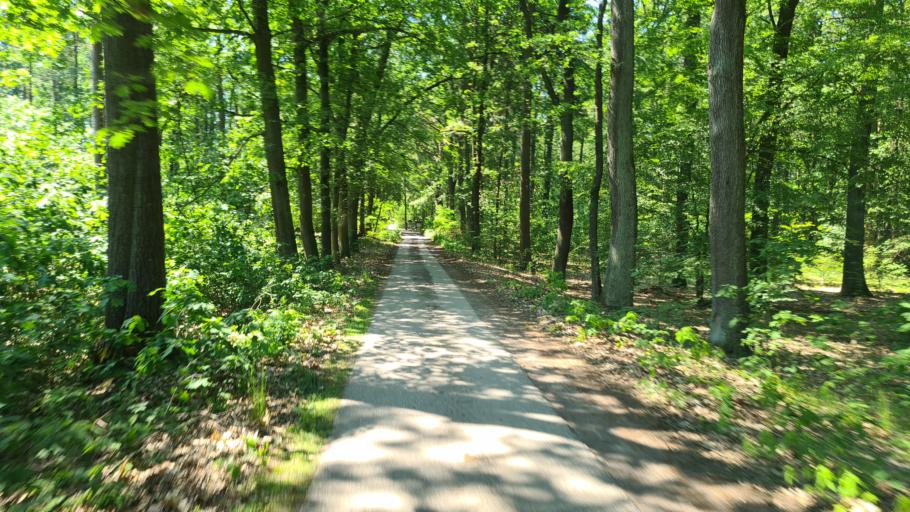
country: DE
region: Brandenburg
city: Lebusa
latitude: 51.7757
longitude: 13.4131
